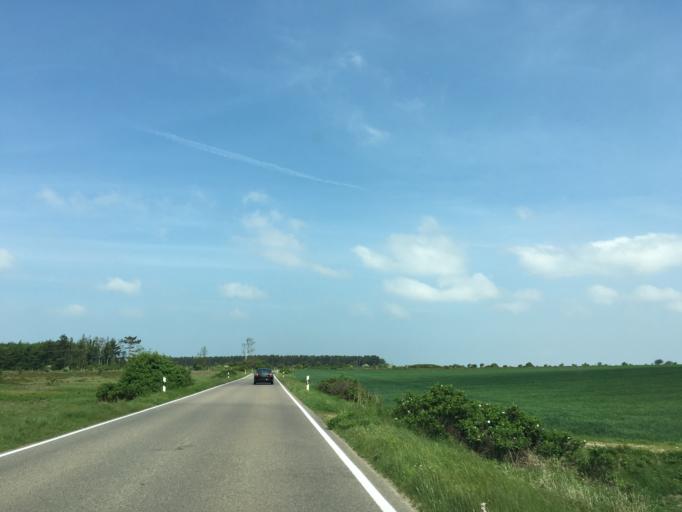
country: DE
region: Schleswig-Holstein
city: Nebel
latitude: 54.6557
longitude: 8.3441
